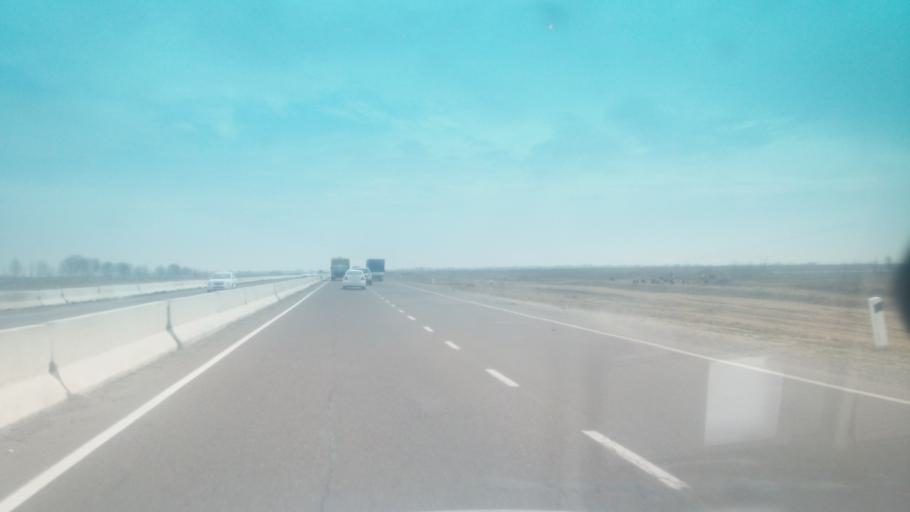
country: KZ
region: Ongtustik Qazaqstan
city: Myrzakent
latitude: 40.5139
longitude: 68.4875
